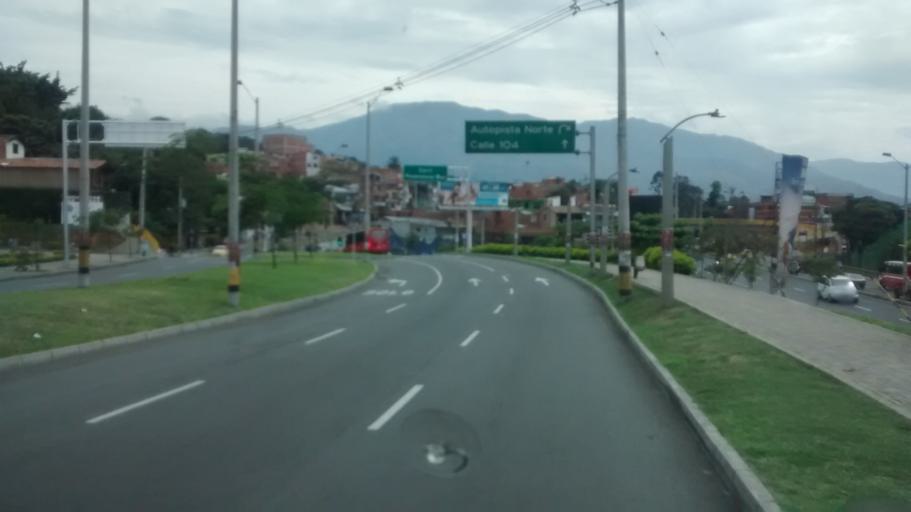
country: CO
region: Antioquia
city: Bello
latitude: 6.2954
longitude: -75.5675
